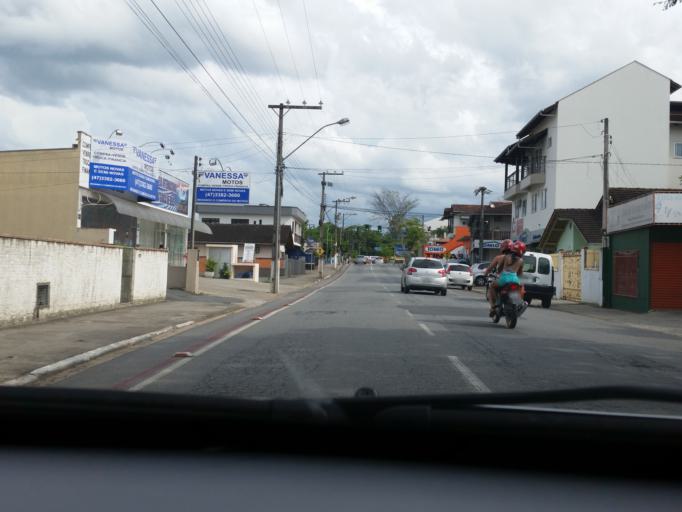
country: BR
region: Santa Catarina
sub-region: Indaial
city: Indaial
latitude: -26.8904
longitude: -49.2437
